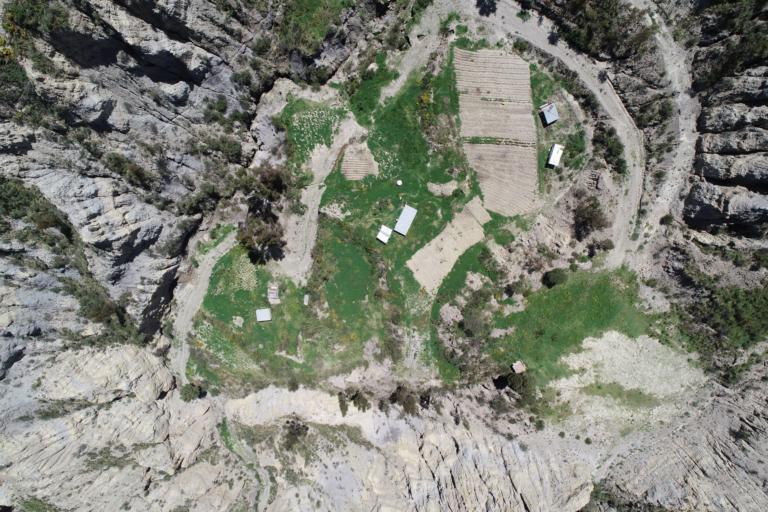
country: BO
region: La Paz
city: La Paz
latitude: -16.5022
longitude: -68.0640
